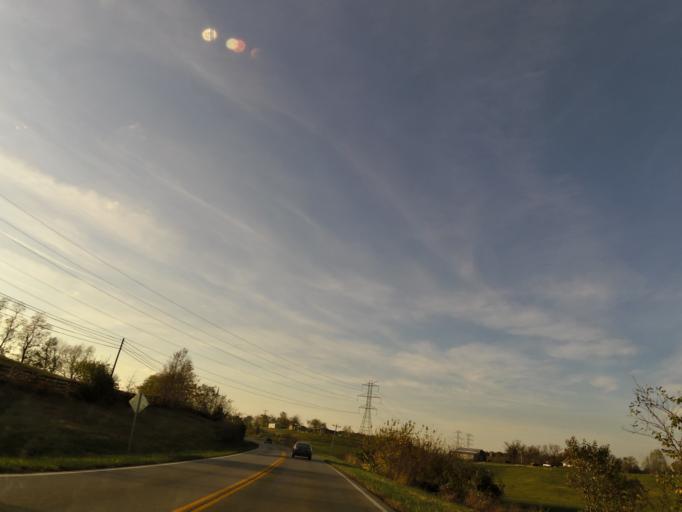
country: US
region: Kentucky
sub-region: Garrard County
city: Lancaster
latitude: 37.6709
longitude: -84.6348
